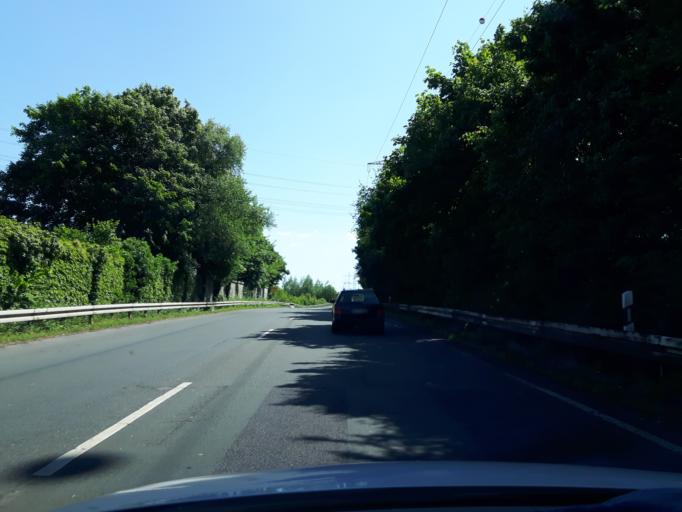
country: DE
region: North Rhine-Westphalia
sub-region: Regierungsbezirk Dusseldorf
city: Ratingen
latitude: 51.3461
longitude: 6.8227
